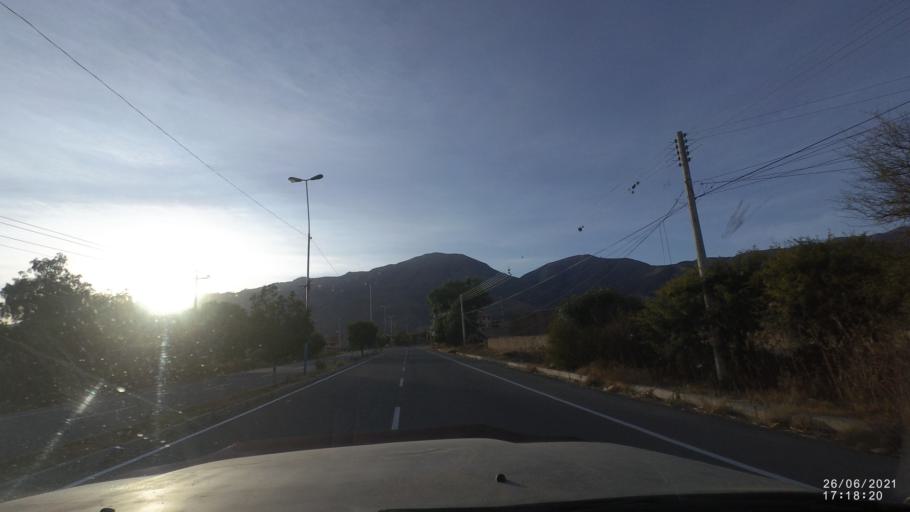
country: BO
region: Cochabamba
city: Cliza
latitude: -17.5372
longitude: -65.9607
